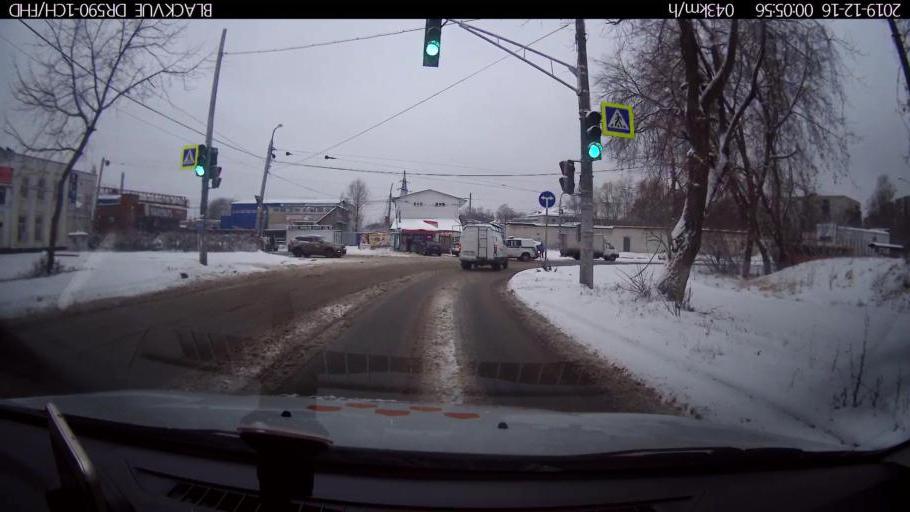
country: RU
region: Nizjnij Novgorod
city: Nizhniy Novgorod
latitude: 56.2716
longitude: 43.9391
